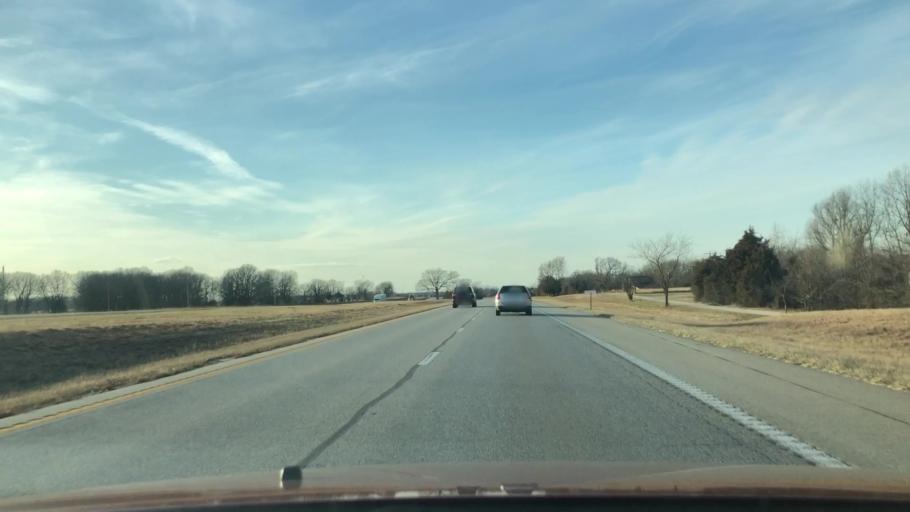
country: US
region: Missouri
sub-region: Webster County
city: Seymour
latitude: 37.1279
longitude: -92.7113
